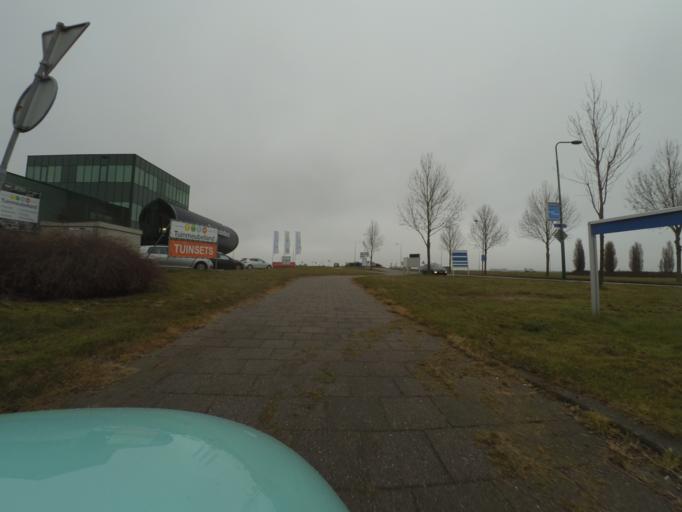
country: NL
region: Flevoland
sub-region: Gemeente Dronten
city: Dronten
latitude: 52.5436
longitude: 5.7102
